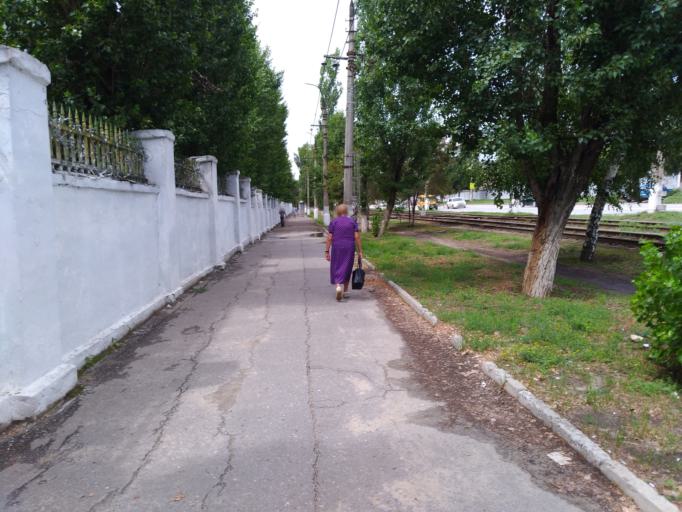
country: RU
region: Volgograd
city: Volgograd
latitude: 48.7165
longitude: 44.4859
